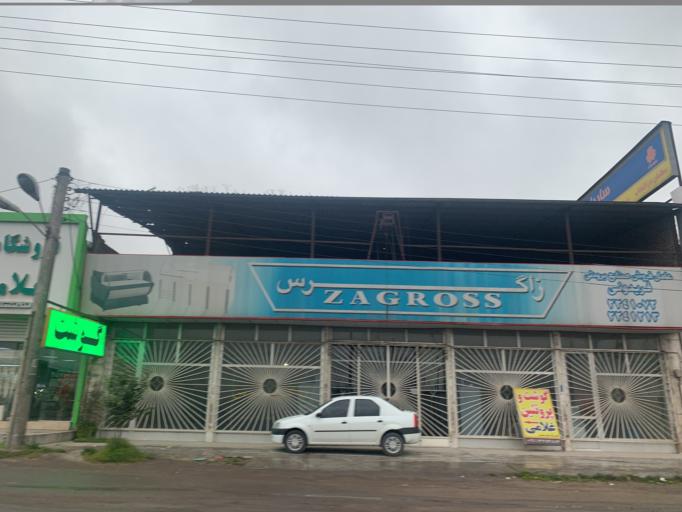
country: IR
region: Mazandaran
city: Amol
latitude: 36.4258
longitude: 52.3499
